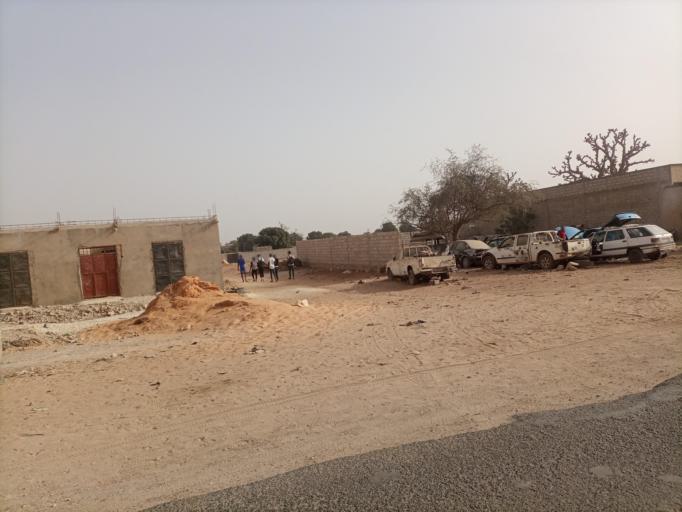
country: SN
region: Thies
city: Nguekhokh
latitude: 14.5843
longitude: -17.0310
